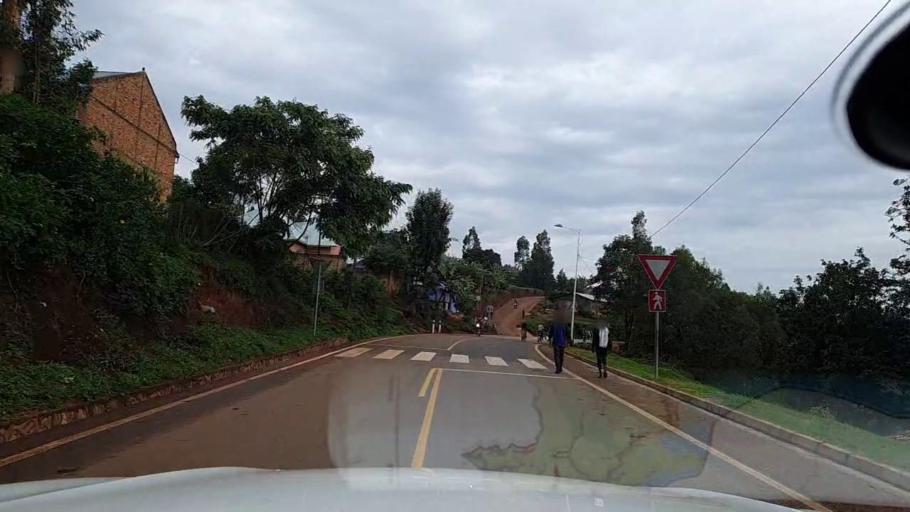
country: RW
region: Southern Province
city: Butare
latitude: -2.5795
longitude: 29.7343
